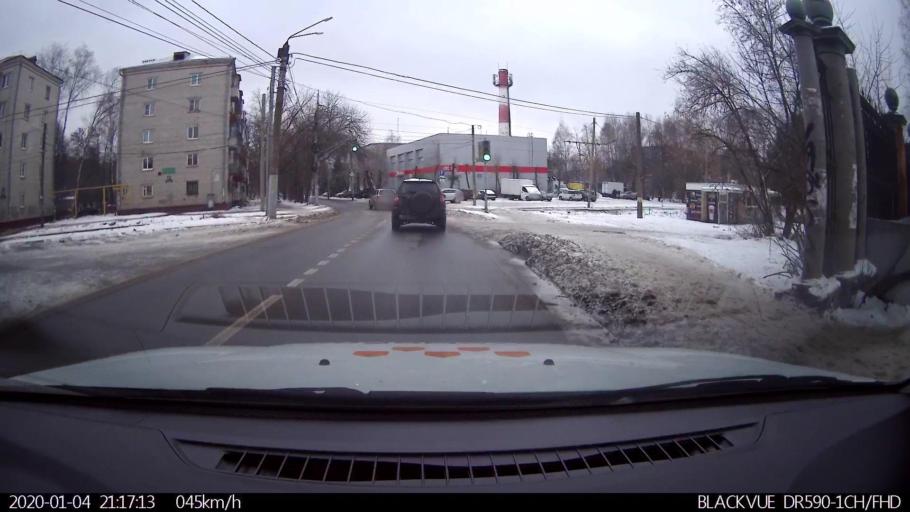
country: RU
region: Nizjnij Novgorod
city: Gorbatovka
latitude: 56.2351
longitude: 43.8521
